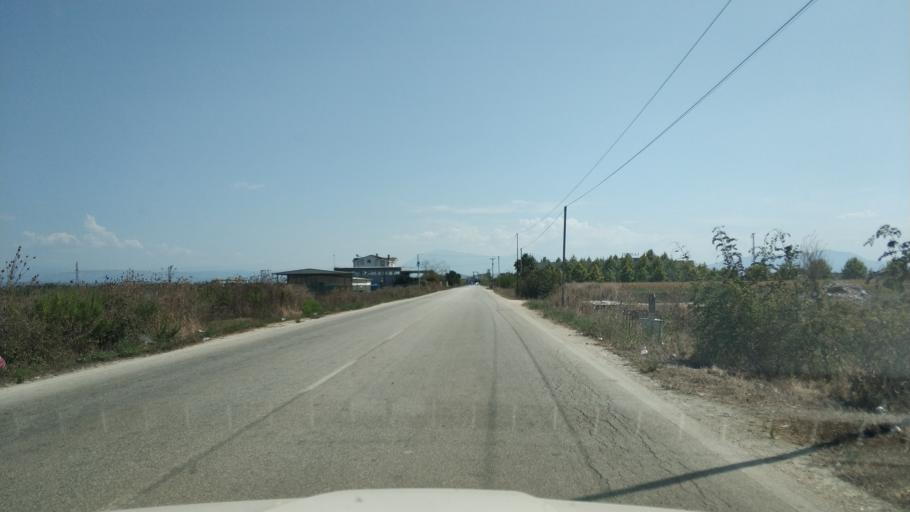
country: AL
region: Fier
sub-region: Rrethi i Lushnjes
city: Krutja e Poshtme
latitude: 40.8814
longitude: 19.6630
